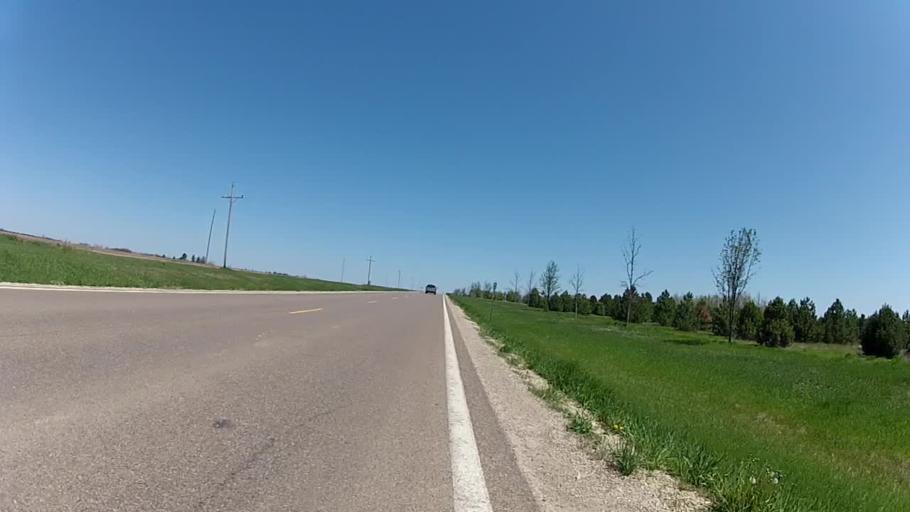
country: US
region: Kansas
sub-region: Riley County
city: Manhattan
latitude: 38.9576
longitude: -96.5201
